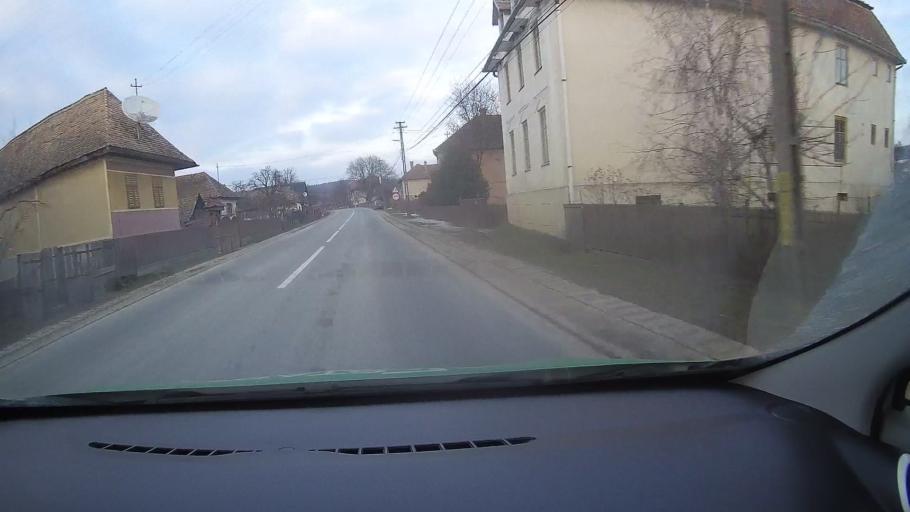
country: RO
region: Harghita
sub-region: Comuna Simonesti
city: Simonesti
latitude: 46.3558
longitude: 25.1394
